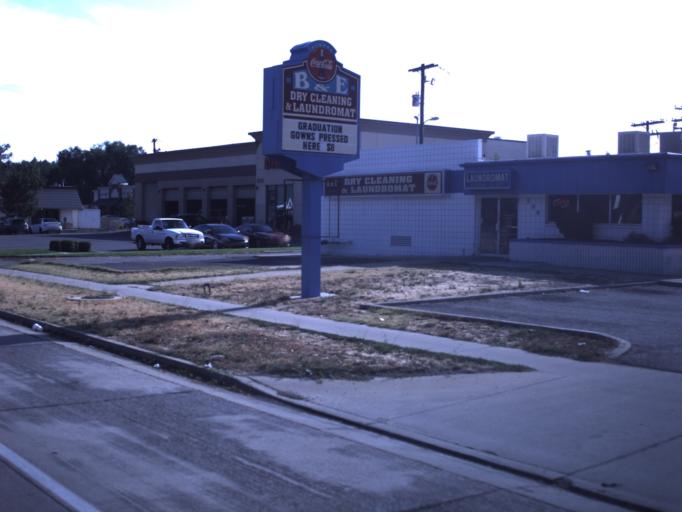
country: US
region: Utah
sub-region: Weber County
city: Ogden
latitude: 41.2535
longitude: -111.9699
